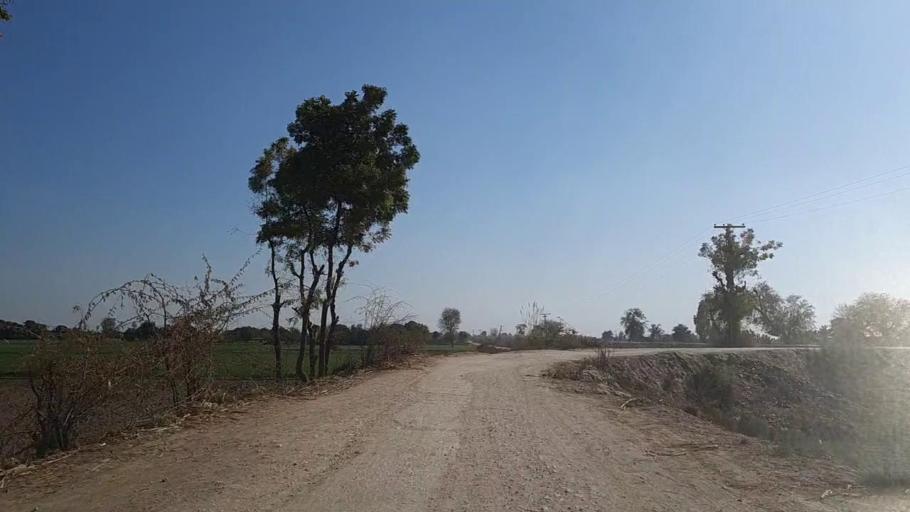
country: PK
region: Sindh
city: Nawabshah
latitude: 26.2251
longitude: 68.4290
